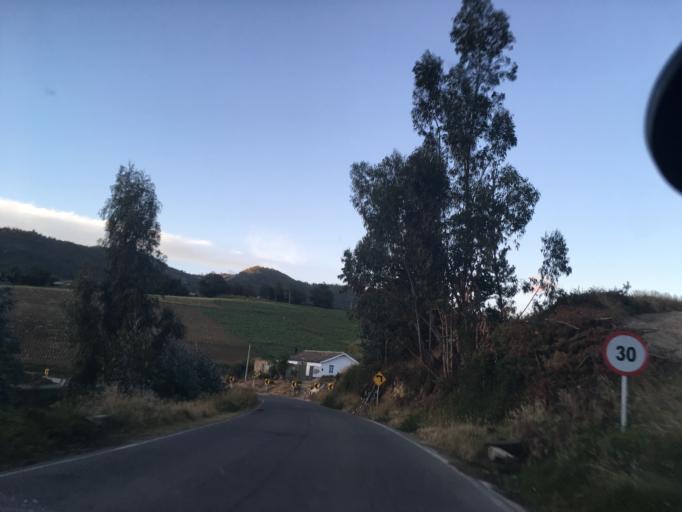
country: CO
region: Boyaca
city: Aquitania
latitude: 5.5823
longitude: -72.8926
